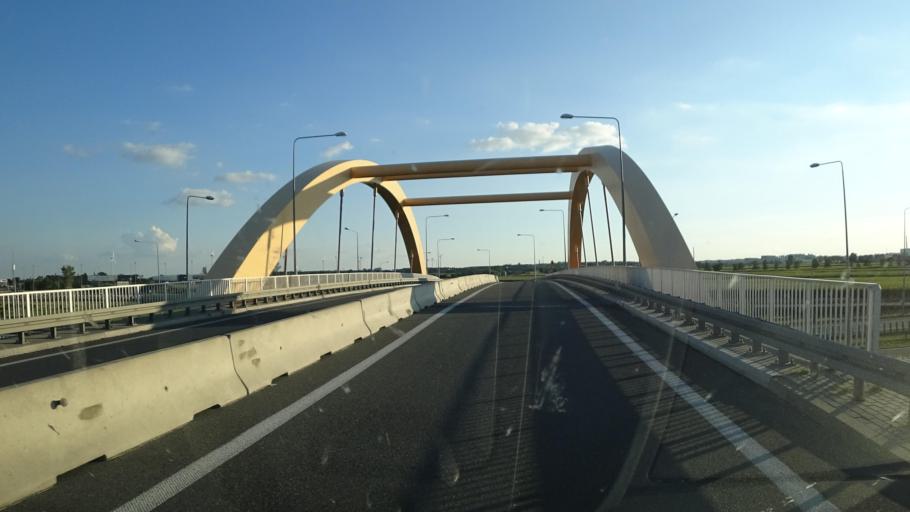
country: PL
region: Lodz Voivodeship
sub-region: Powiat kutnowski
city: Krzyzanow
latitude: 52.2252
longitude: 19.4661
